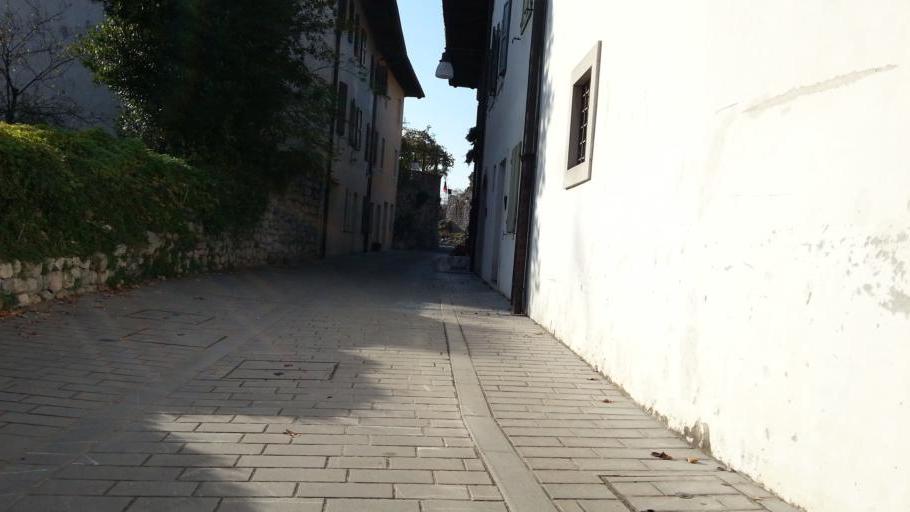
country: IT
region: Friuli Venezia Giulia
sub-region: Provincia di Udine
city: Venzone
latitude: 46.3337
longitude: 13.1384
